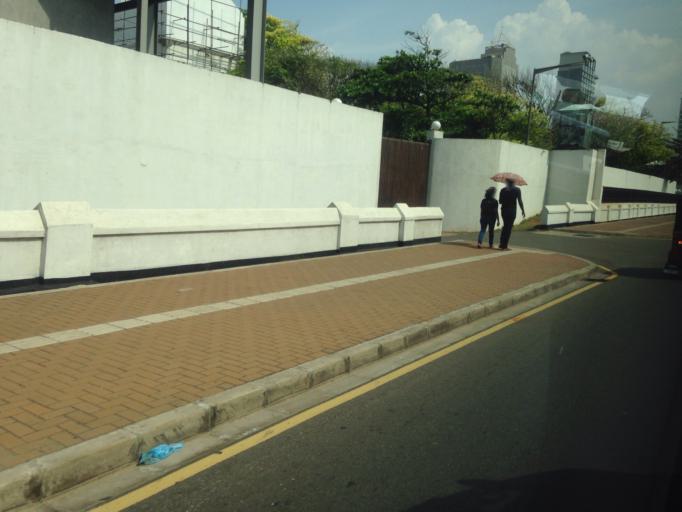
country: LK
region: Western
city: Colombo
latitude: 6.9156
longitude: 79.8484
